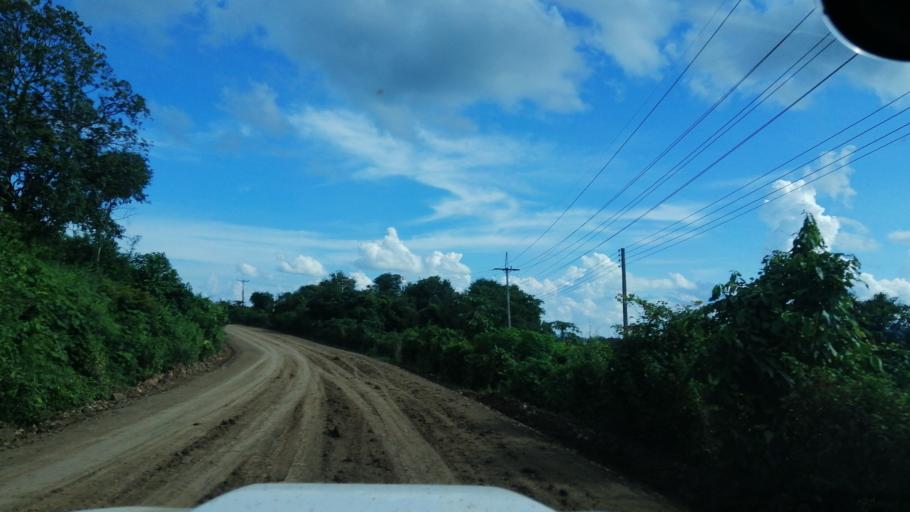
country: TH
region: Uttaradit
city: Ban Khok
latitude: 17.8700
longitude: 101.2207
